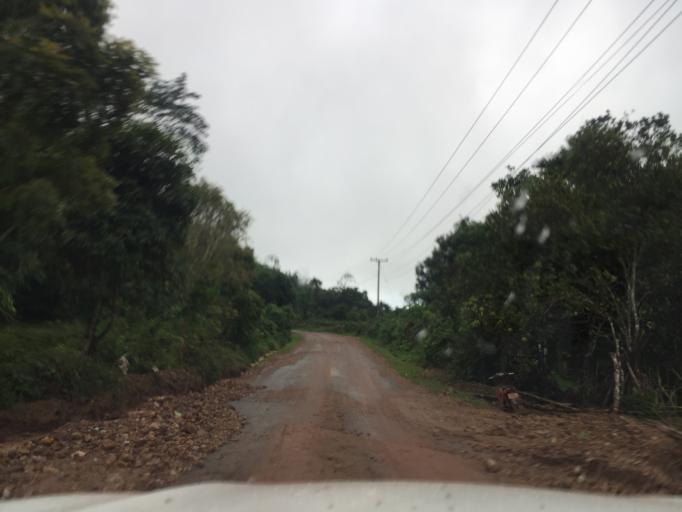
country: LA
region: Oudomxai
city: Muang La
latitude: 20.8296
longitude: 102.0981
